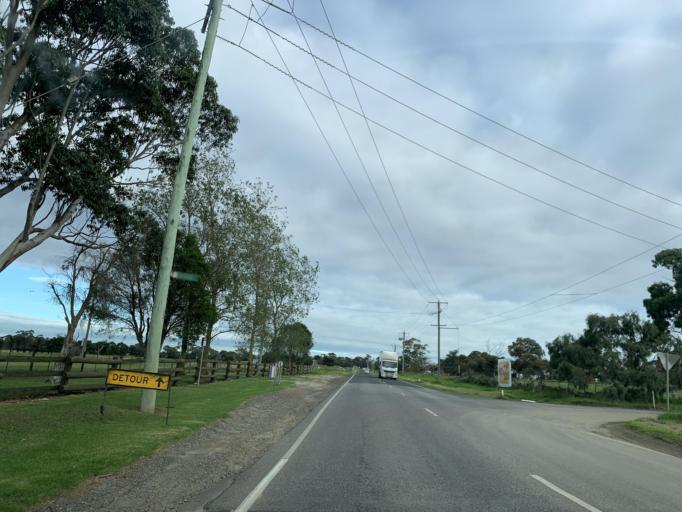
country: AU
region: Victoria
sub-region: Casey
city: Junction Village
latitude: -38.1358
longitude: 145.3434
